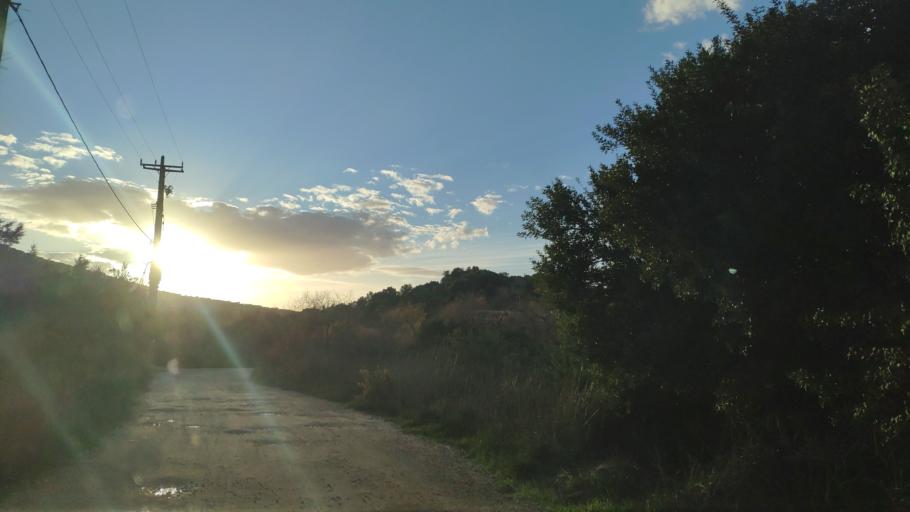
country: GR
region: Attica
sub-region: Nomarchia Anatolikis Attikis
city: Limin Mesoyaias
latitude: 37.9247
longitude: 23.9991
